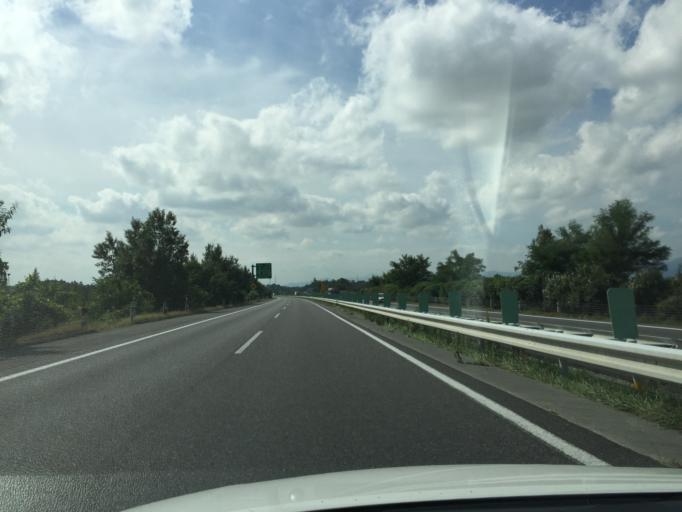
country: JP
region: Fukushima
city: Motomiya
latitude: 37.4797
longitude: 140.3694
